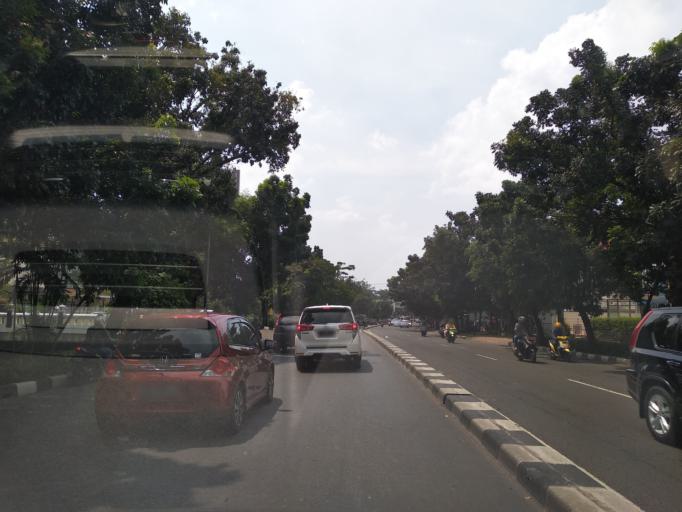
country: ID
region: Jakarta Raya
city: Jakarta
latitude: -6.2259
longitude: 106.8474
